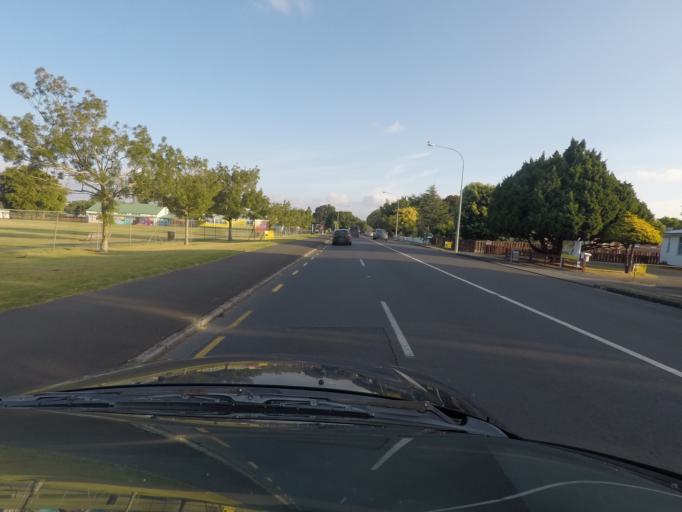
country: NZ
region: Auckland
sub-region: Auckland
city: Rosebank
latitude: -36.8877
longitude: 174.6851
